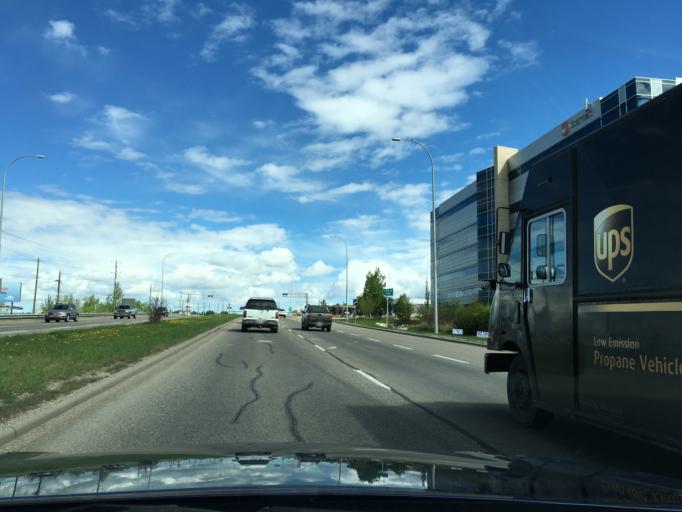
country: CA
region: Alberta
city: Calgary
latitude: 51.0482
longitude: -114.0016
